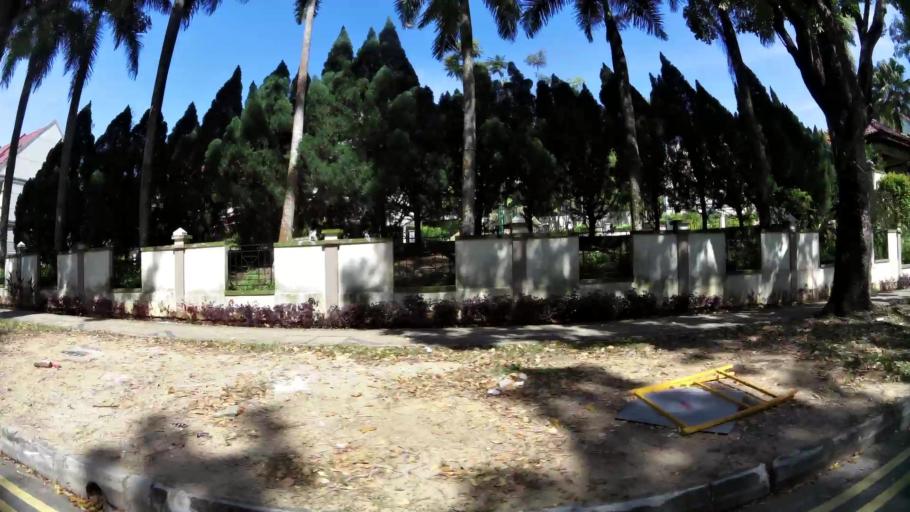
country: SG
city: Singapore
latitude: 1.3772
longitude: 103.8353
